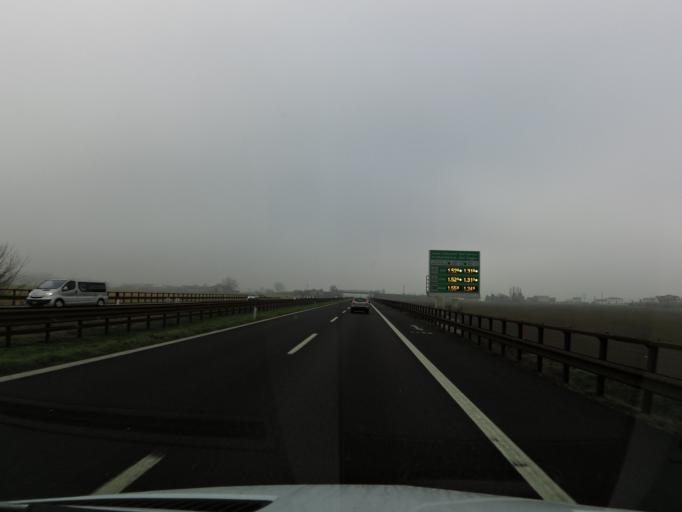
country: IT
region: Lombardy
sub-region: Provincia di Mantova
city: Pegognaga
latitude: 45.0261
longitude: 10.8539
